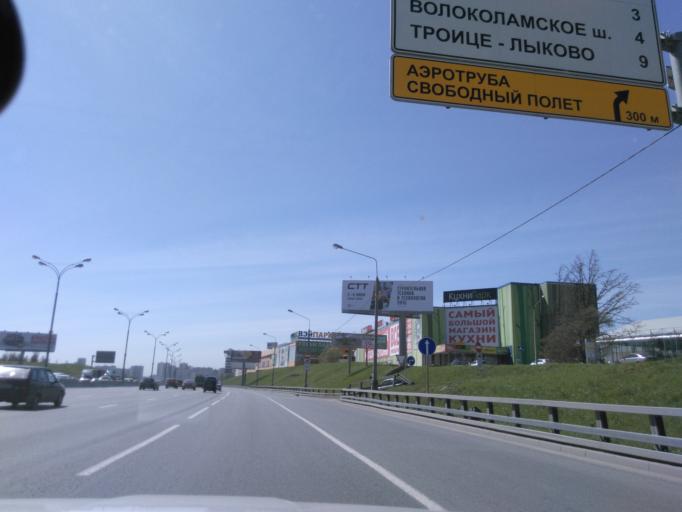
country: RU
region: Moscow
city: Strogino
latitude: 55.8614
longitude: 37.3990
